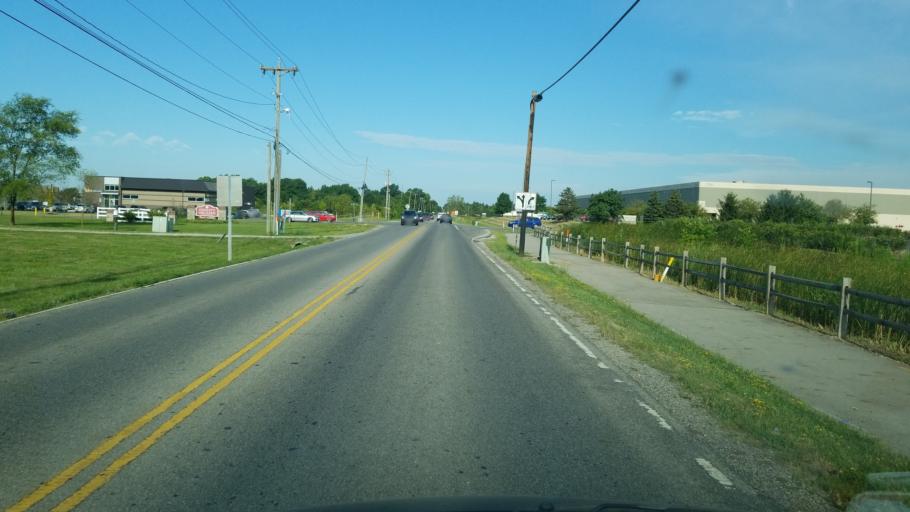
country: US
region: Ohio
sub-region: Delaware County
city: Lewis Center
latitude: 40.1747
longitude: -83.0093
